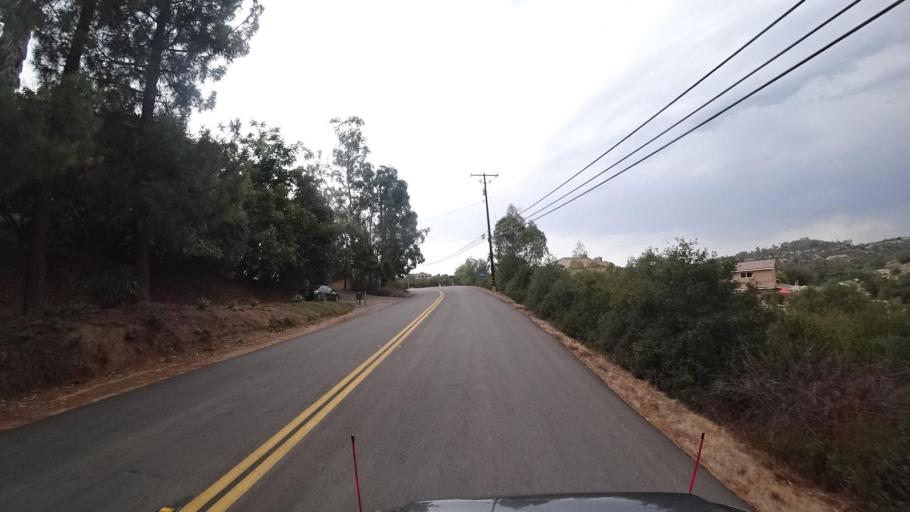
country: US
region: California
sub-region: San Diego County
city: San Pasqual
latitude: 33.0321
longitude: -116.9636
